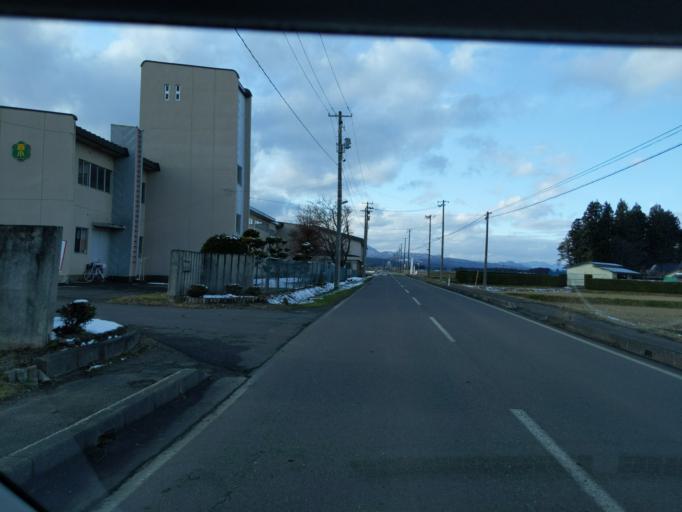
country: JP
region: Iwate
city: Mizusawa
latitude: 39.1971
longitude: 141.0683
